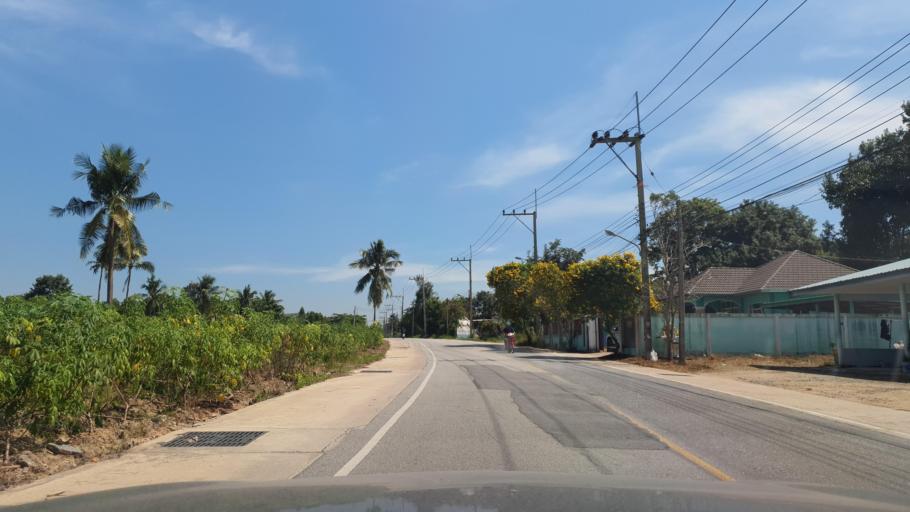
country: TH
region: Chon Buri
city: Bang Lamung
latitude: 12.9838
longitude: 100.9724
